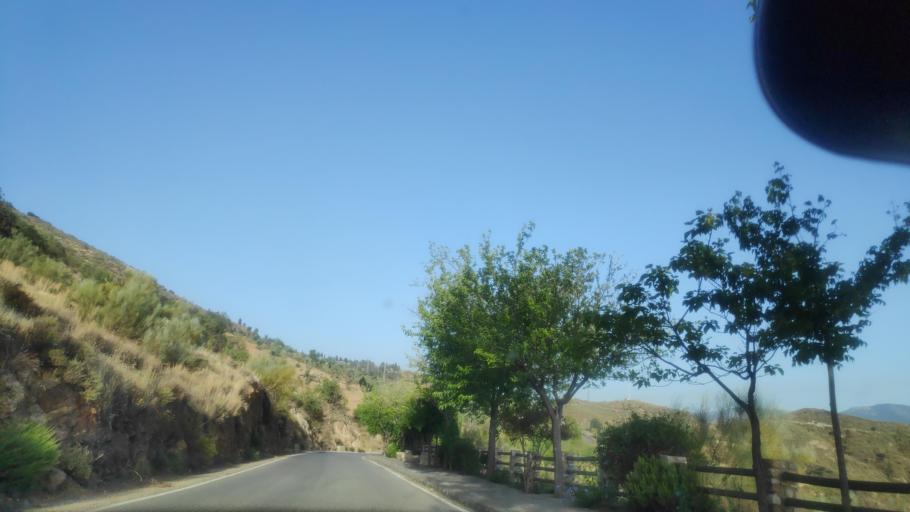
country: ES
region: Andalusia
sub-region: Provincia de Granada
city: Soportujar
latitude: 36.9255
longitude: -3.3983
